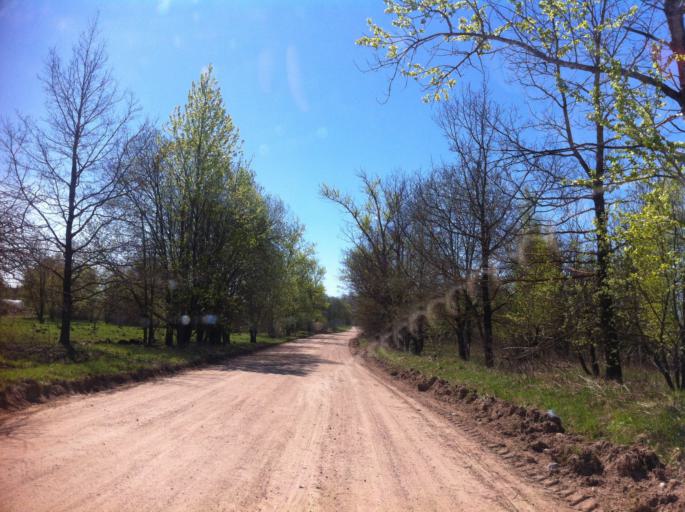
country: RU
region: Pskov
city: Izborsk
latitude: 57.7870
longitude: 27.9626
